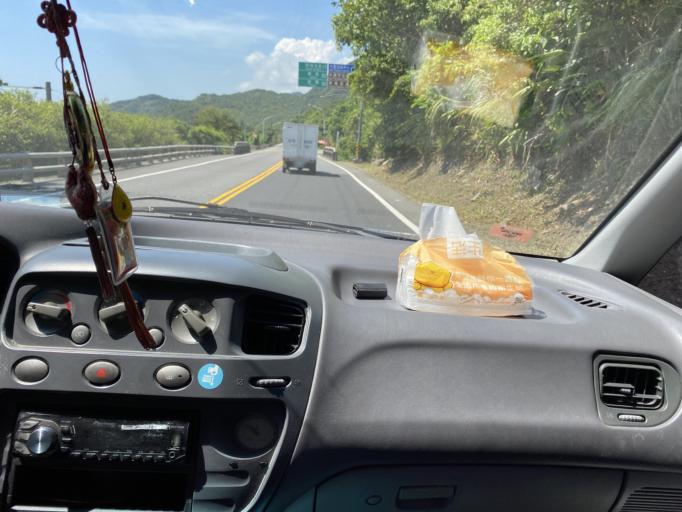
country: TW
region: Taiwan
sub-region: Keelung
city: Keelung
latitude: 24.9714
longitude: 121.9281
